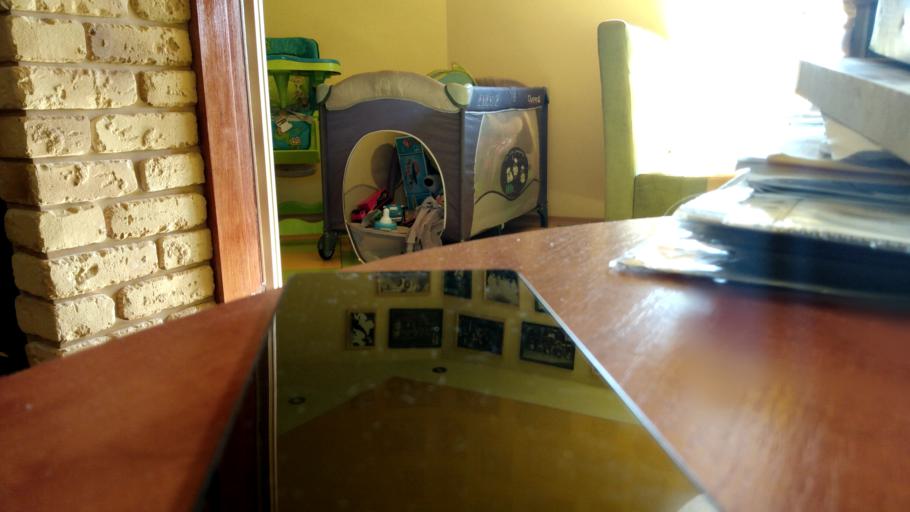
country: RU
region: Penza
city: Serdobsk
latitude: 52.4655
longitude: 44.2814
